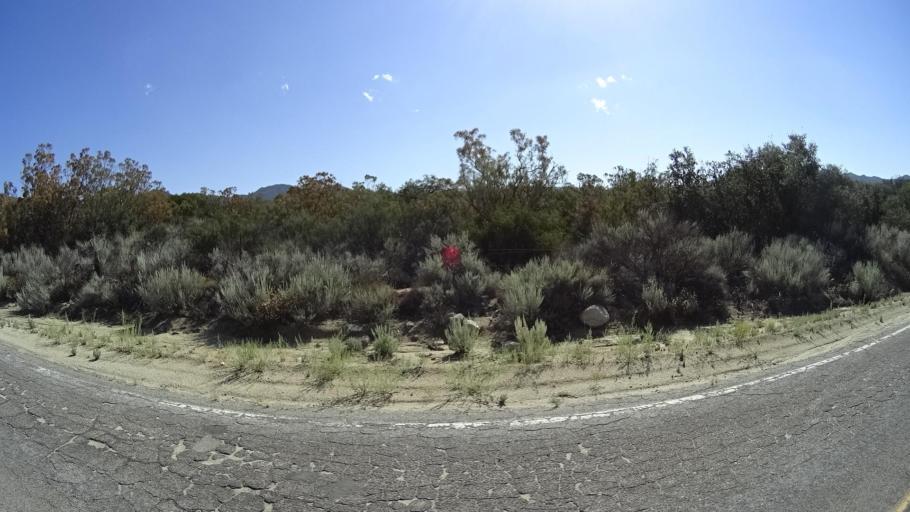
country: US
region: California
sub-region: Riverside County
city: Anza
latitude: 33.3805
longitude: -116.6521
